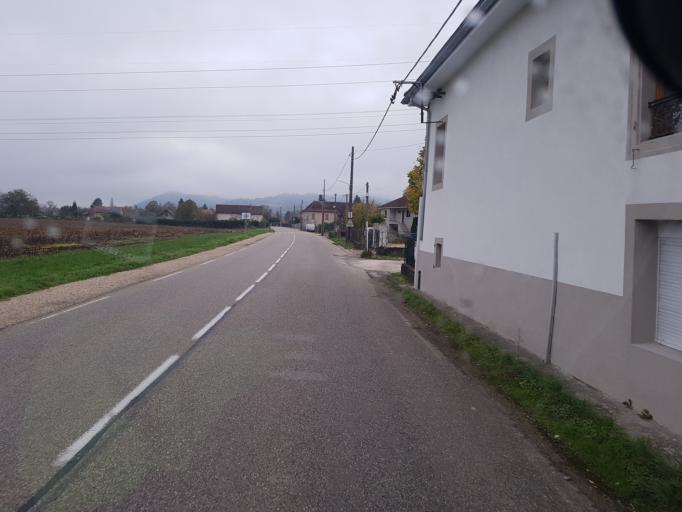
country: FR
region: Rhone-Alpes
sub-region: Departement de l'Isere
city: Aoste
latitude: 45.5909
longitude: 5.6146
